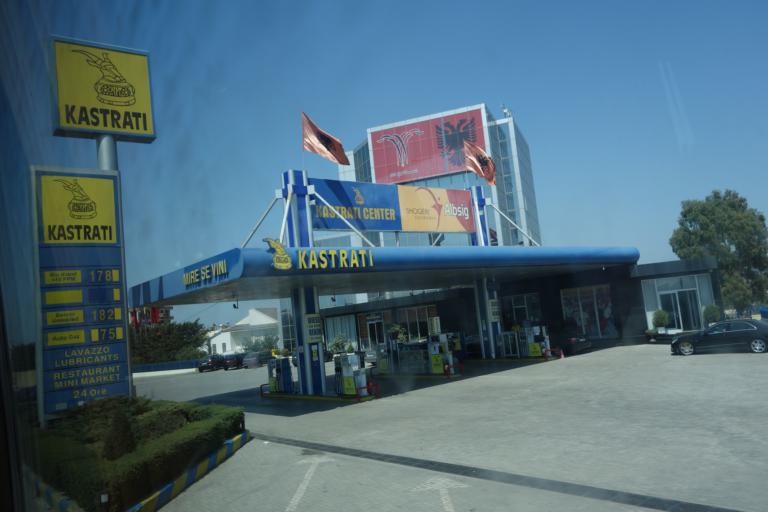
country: AL
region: Durres
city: Durres
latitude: 41.3214
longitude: 19.4705
